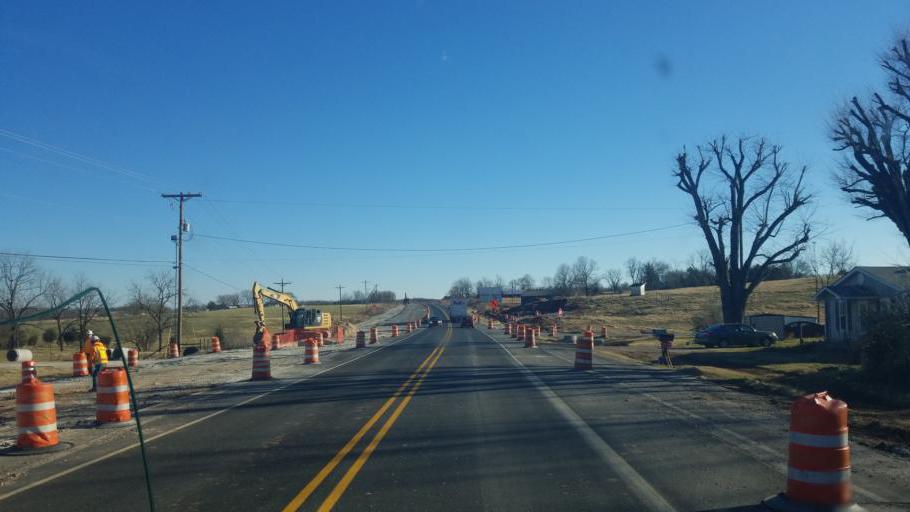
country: US
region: Arkansas
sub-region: Boone County
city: Harrison
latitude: 36.1532
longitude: -92.9900
